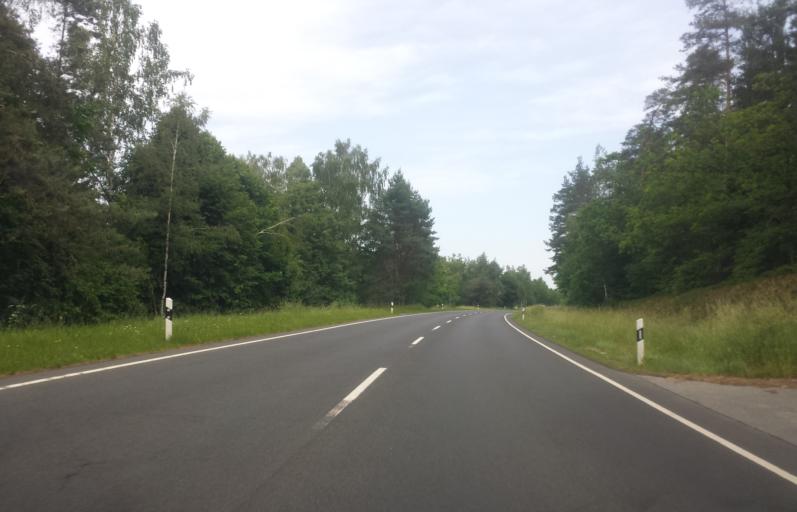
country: DE
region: Bavaria
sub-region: Upper Palatinate
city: Pressath
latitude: 49.7563
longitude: 11.9216
